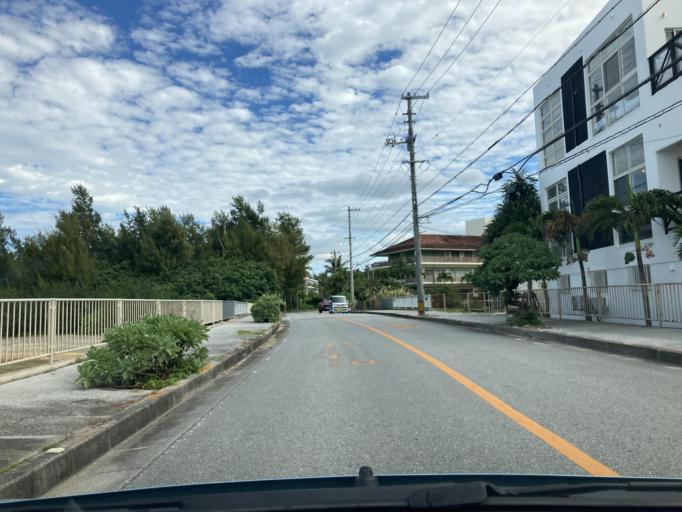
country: JP
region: Okinawa
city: Ishikawa
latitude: 26.4313
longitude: 127.7560
